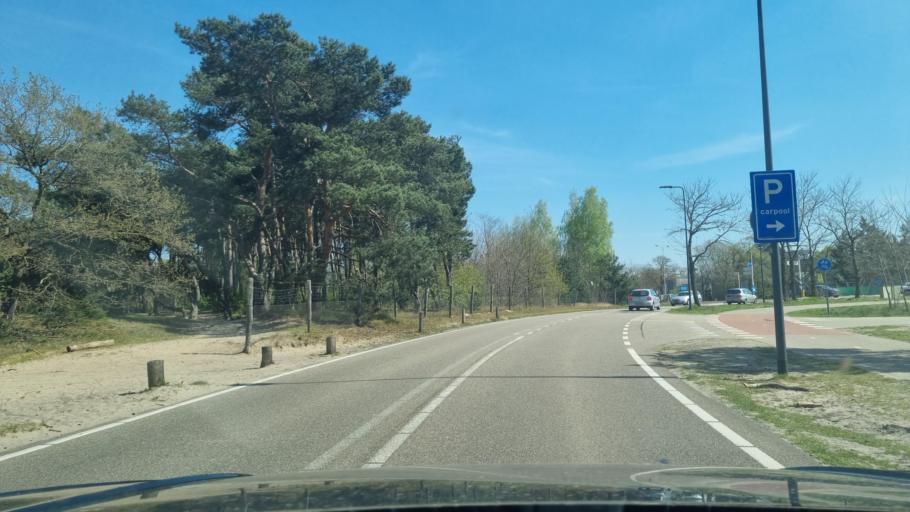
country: NL
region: North Brabant
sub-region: Gemeente Sint-Michielsgestel
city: Sint-Michielsgestel
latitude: 51.7096
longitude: 5.3804
